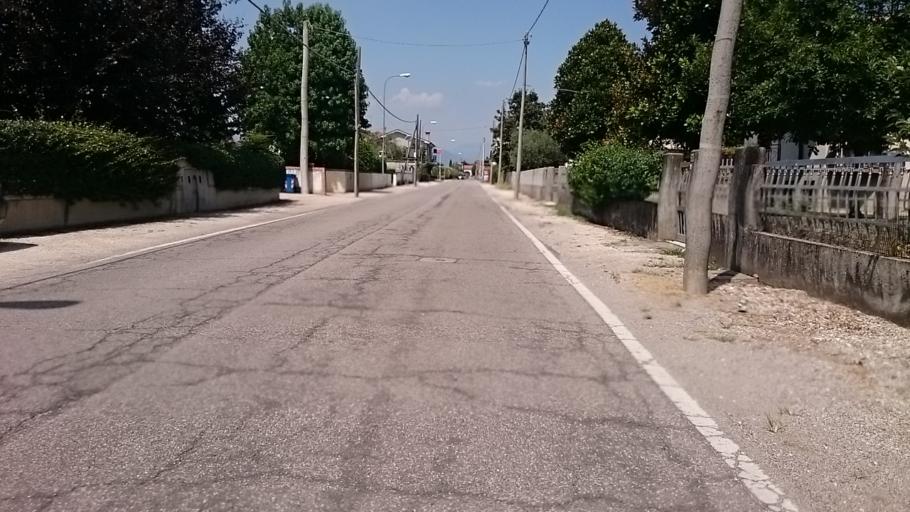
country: IT
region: Veneto
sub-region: Provincia di Padova
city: Fontaniva
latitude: 45.6582
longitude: 11.7573
